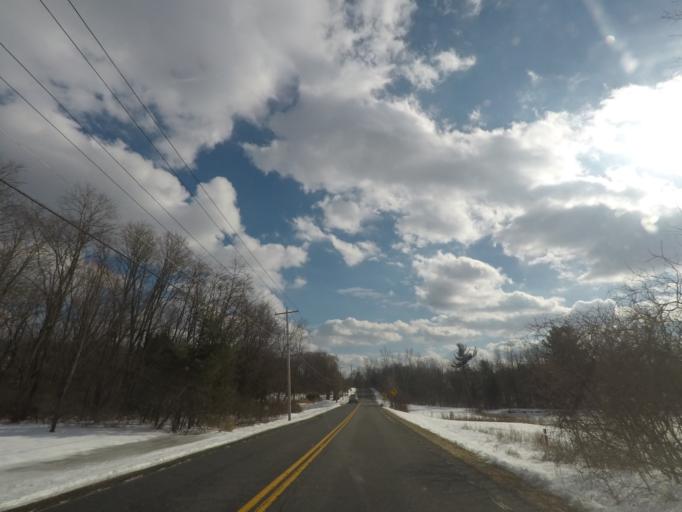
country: US
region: New York
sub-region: Schenectady County
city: Niskayuna
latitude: 42.8352
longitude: -73.8698
